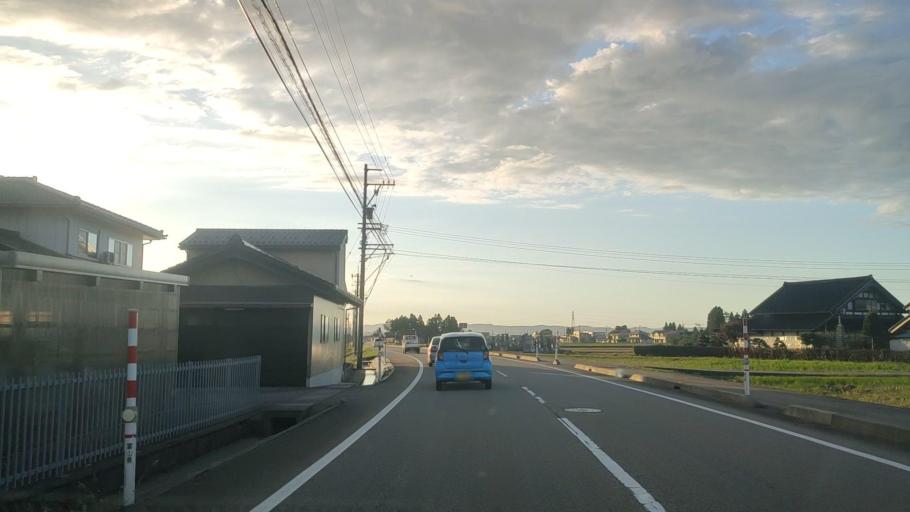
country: JP
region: Toyama
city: Nanto-shi
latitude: 36.5989
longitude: 136.9435
